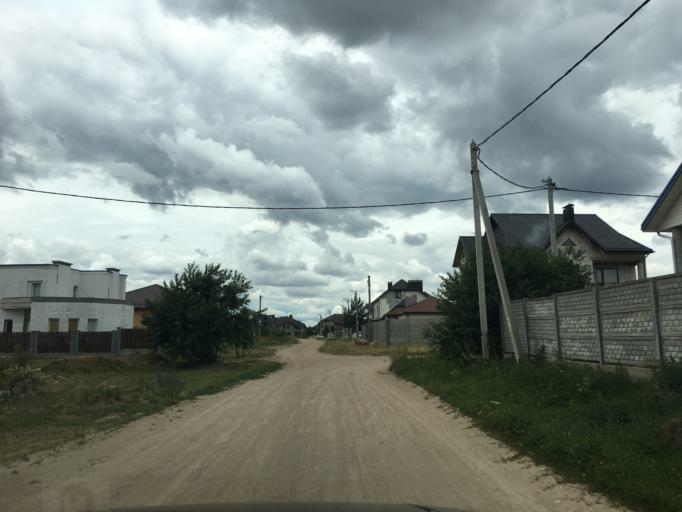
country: BY
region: Grodnenskaya
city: Hrodna
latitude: 53.6182
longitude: 23.8300
